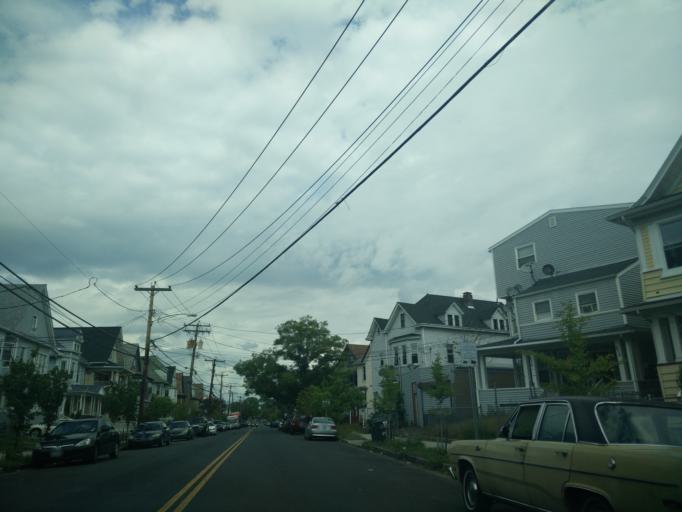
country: US
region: Connecticut
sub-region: Fairfield County
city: Bridgeport
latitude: 41.1694
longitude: -73.2011
